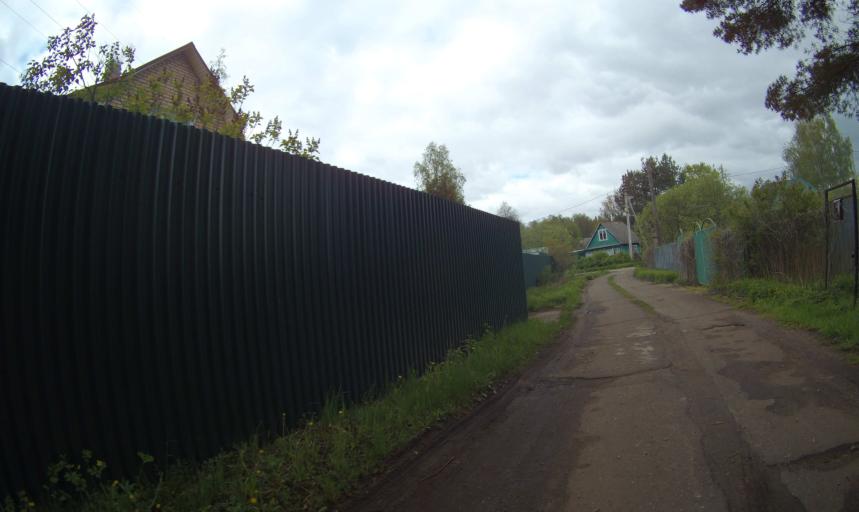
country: RU
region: Moskovskaya
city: Rechitsy
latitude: 55.5528
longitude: 38.4825
